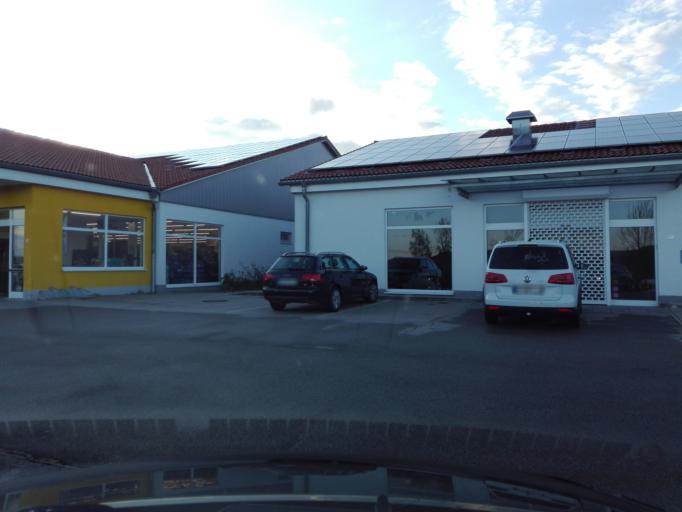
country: DE
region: Bavaria
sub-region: Lower Bavaria
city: Wegscheid
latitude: 48.5952
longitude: 13.7811
